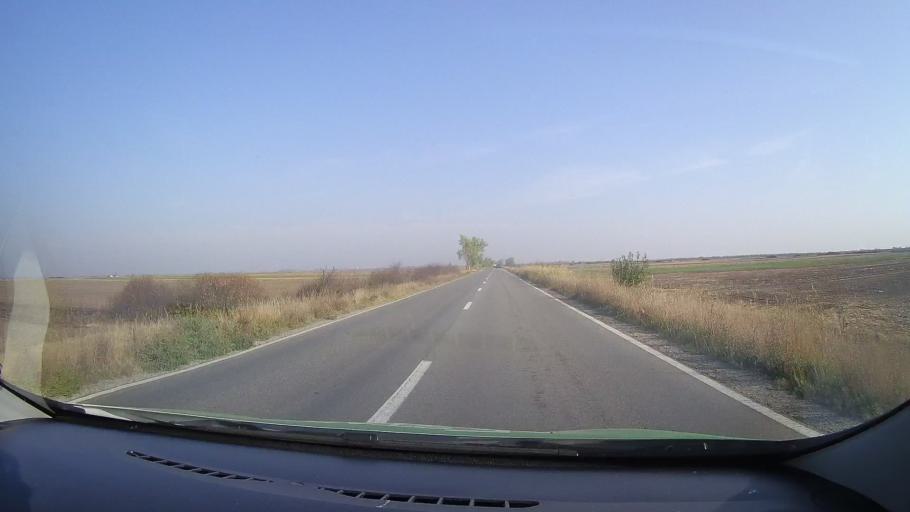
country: RO
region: Arad
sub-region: Comuna Pilu
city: Pilu
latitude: 46.5902
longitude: 21.3462
